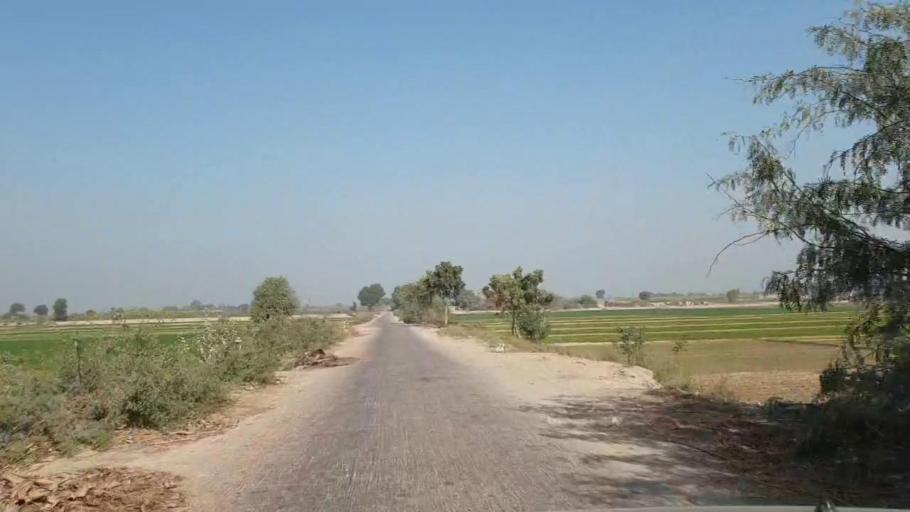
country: PK
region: Sindh
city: Tando Allahyar
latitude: 25.5588
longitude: 68.6080
